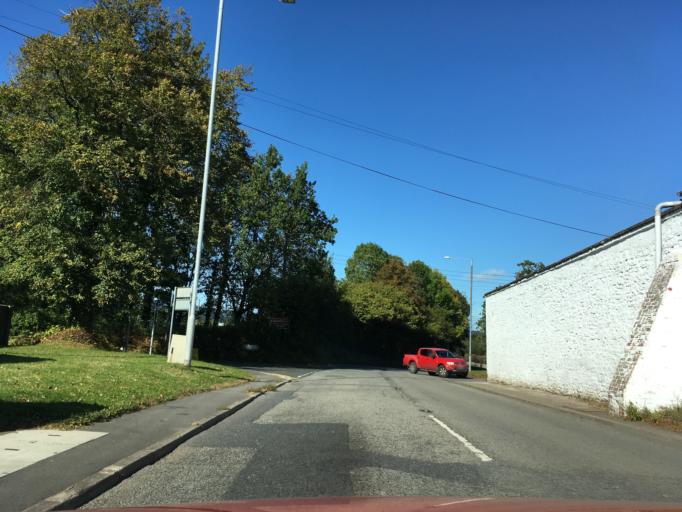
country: GB
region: Wales
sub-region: Torfaen County Borough
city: Cwmbran
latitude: 51.6262
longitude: -3.0091
